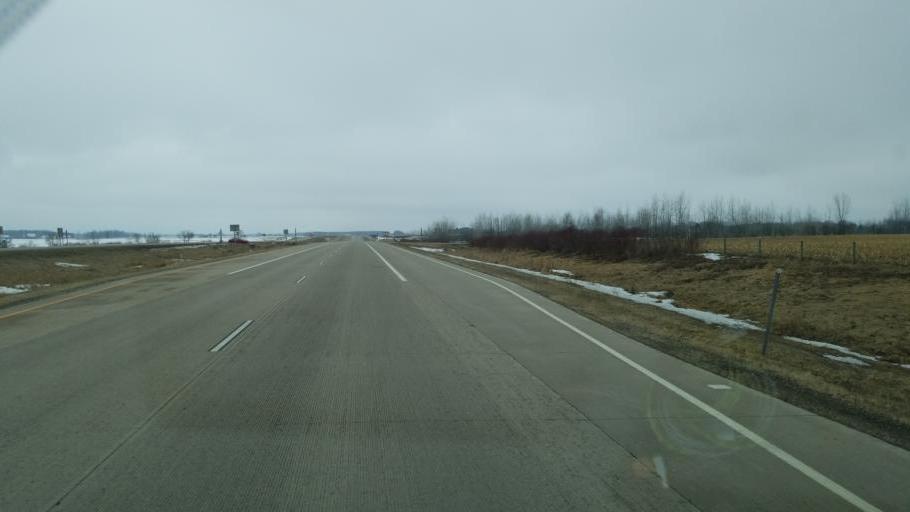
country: US
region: Wisconsin
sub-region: Wood County
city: Marshfield
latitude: 44.6203
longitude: -90.0029
